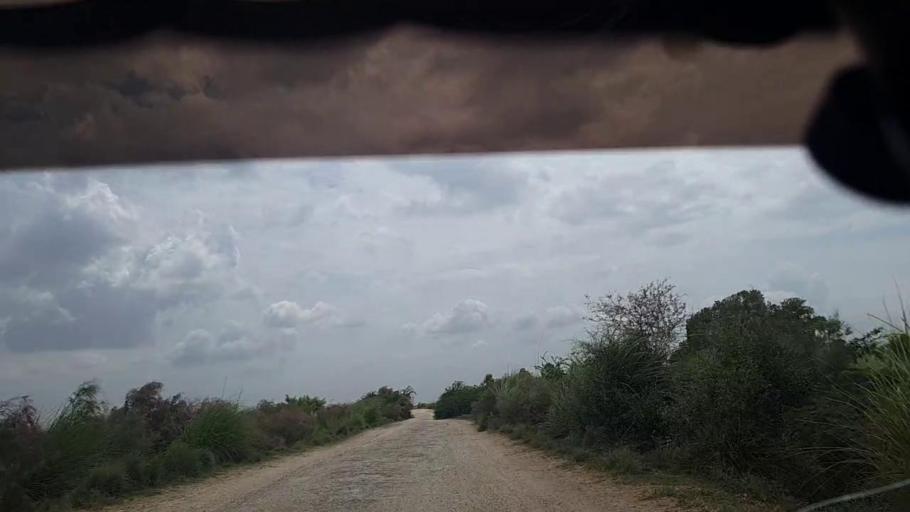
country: PK
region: Sindh
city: Rustam jo Goth
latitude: 28.0553
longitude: 68.9396
